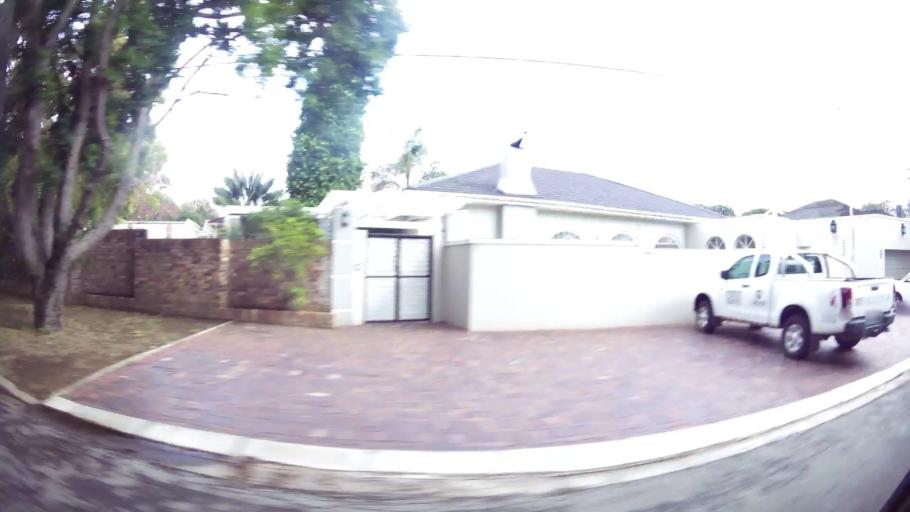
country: ZA
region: Eastern Cape
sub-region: Nelson Mandela Bay Metropolitan Municipality
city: Port Elizabeth
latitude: -33.9650
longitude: 25.5956
